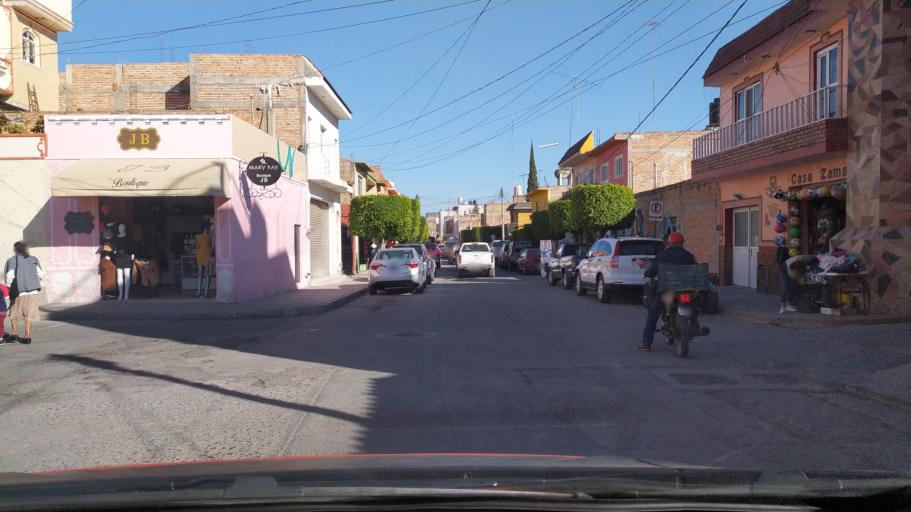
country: MX
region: Guanajuato
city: Ciudad Manuel Doblado
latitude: 20.7266
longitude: -101.9529
